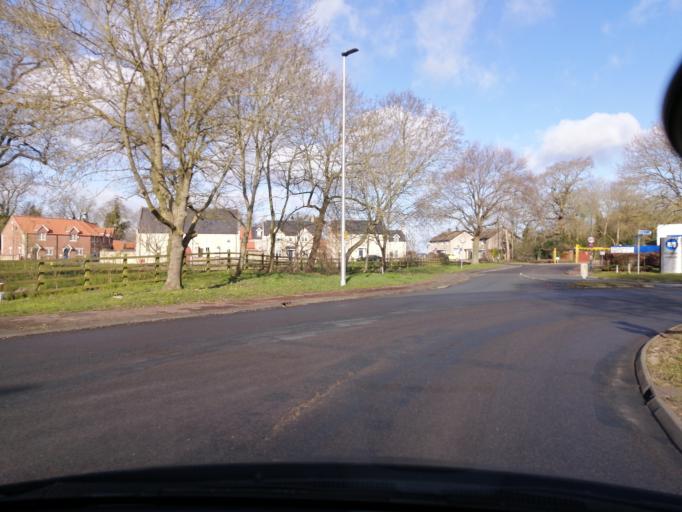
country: GB
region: England
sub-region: Peterborough
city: Marholm
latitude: 52.5879
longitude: -0.2861
